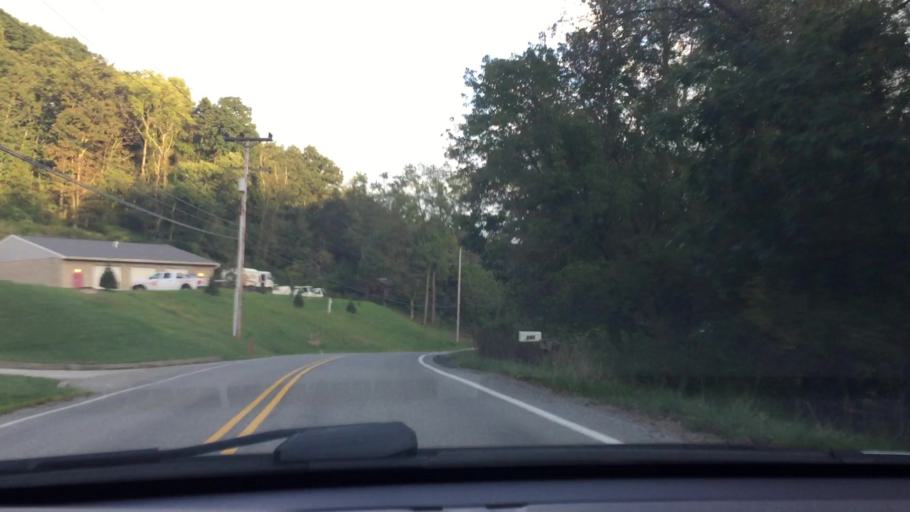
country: US
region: Pennsylvania
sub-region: Westmoreland County
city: Murrysville
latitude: 40.4502
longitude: -79.7248
